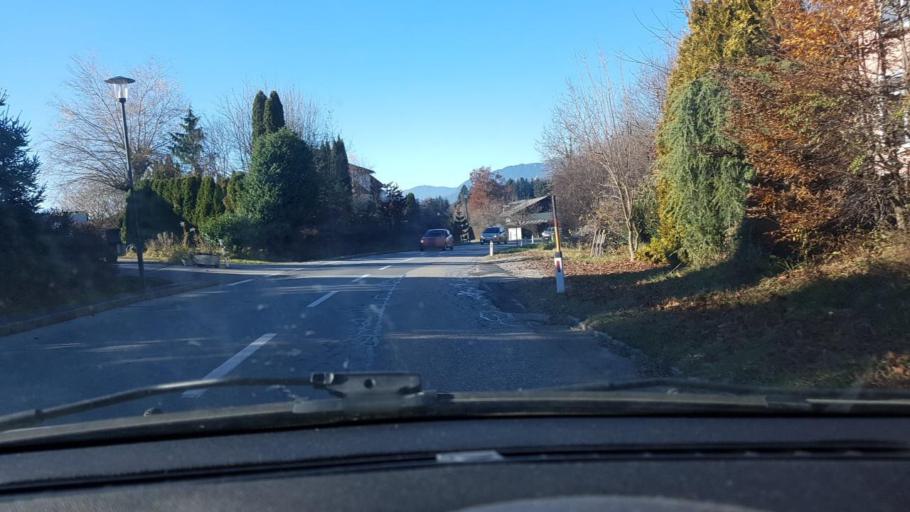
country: AT
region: Carinthia
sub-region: Politischer Bezirk Villach Land
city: Velden am Woerthersee
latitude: 46.6026
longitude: 14.0380
